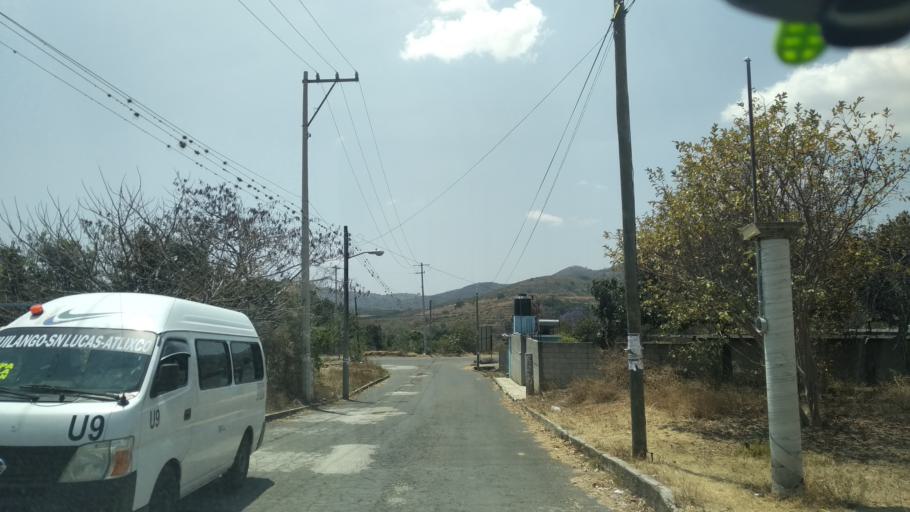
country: MX
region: Puebla
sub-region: Atzitzihuacan
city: Santiago Atzitzihuacan
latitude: 18.8366
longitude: -98.5955
